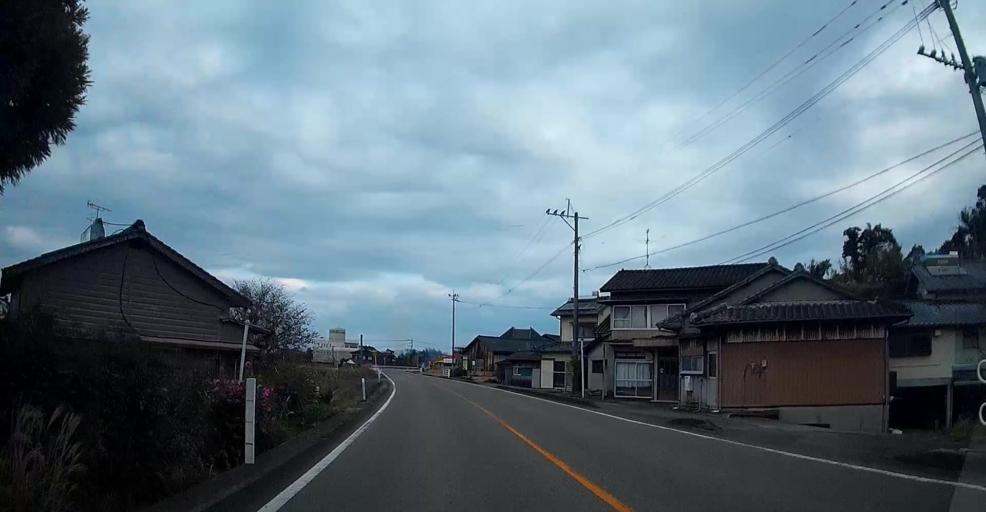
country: JP
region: Kumamoto
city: Hondo
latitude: 32.4753
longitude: 130.2603
